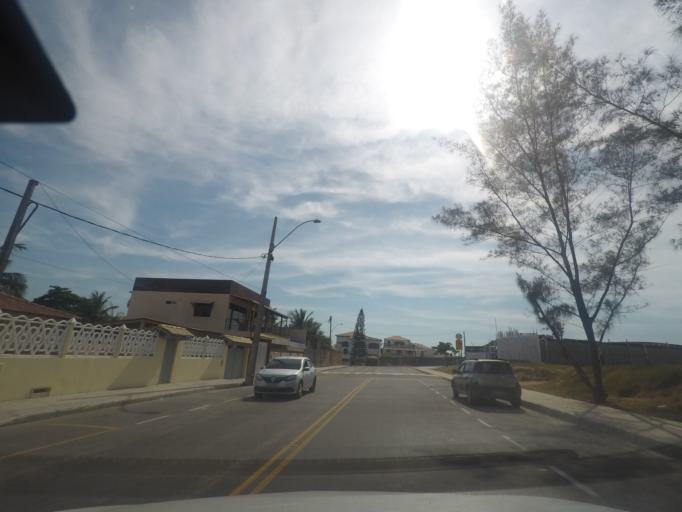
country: BR
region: Rio de Janeiro
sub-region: Marica
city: Marica
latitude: -22.9608
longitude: -42.8173
